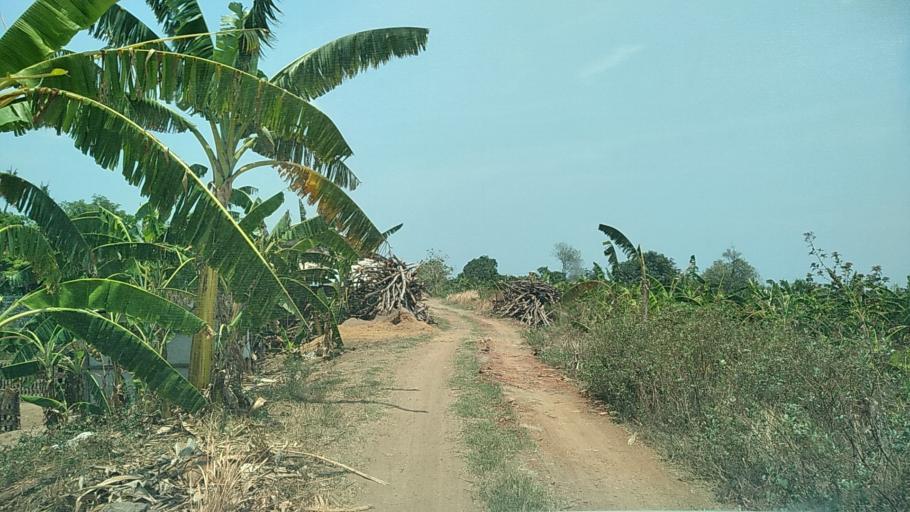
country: ID
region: Central Java
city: Mranggen
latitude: -6.9567
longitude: 110.4935
